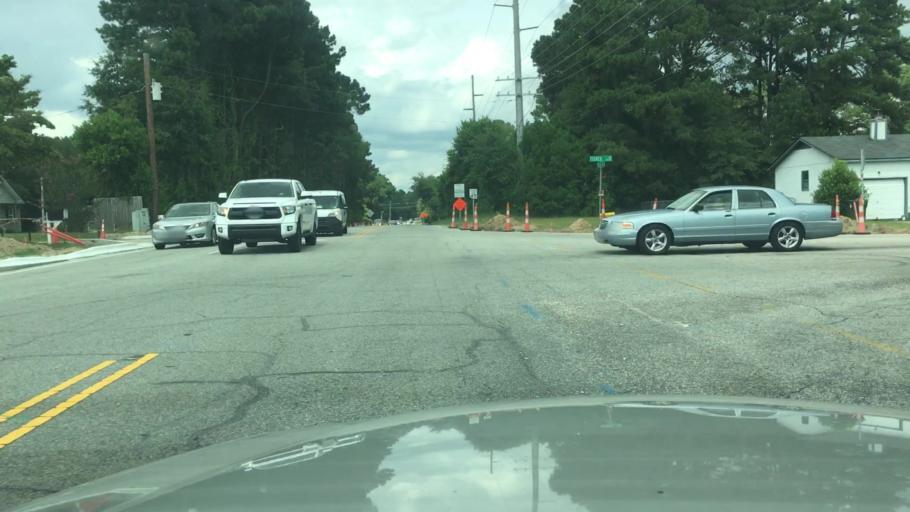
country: US
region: North Carolina
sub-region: Hoke County
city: Rockfish
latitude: 35.0158
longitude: -79.0079
